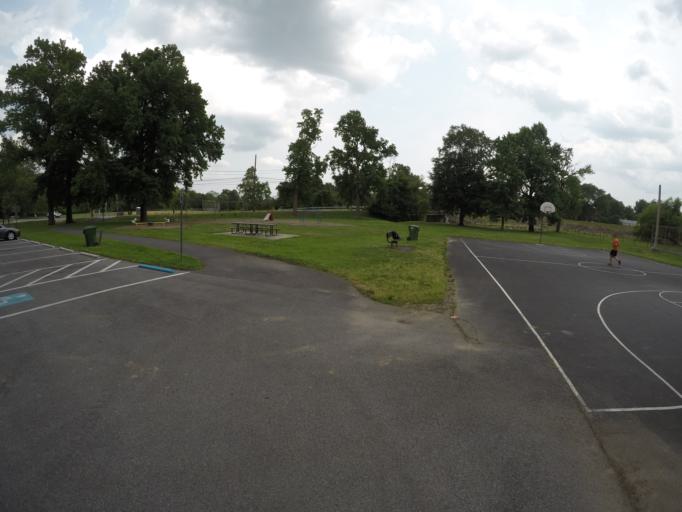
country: US
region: Maryland
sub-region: Prince George's County
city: Brentwood
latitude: 38.9499
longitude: -76.9569
